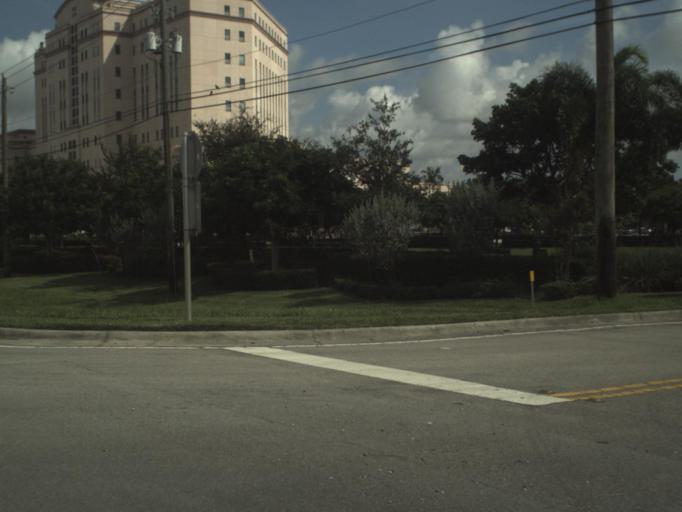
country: US
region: Florida
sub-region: Palm Beach County
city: Mangonia Park
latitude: 26.7824
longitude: -80.1111
